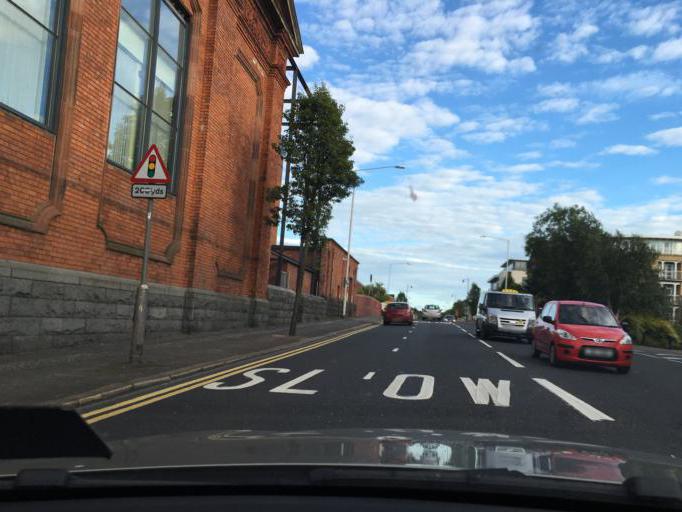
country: GB
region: Northern Ireland
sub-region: City of Belfast
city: Belfast
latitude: 54.5893
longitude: -5.9247
